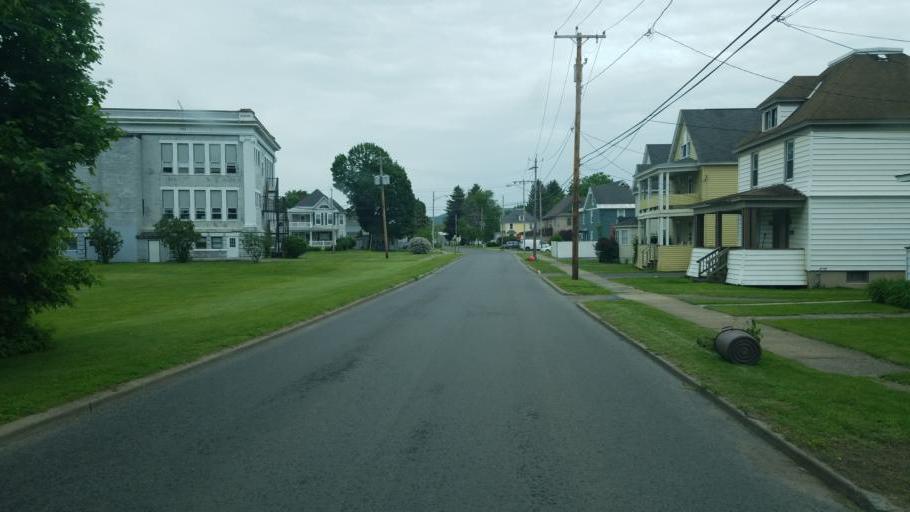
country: US
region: New York
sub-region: Herkimer County
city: Herkimer
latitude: 43.0341
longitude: -74.9890
